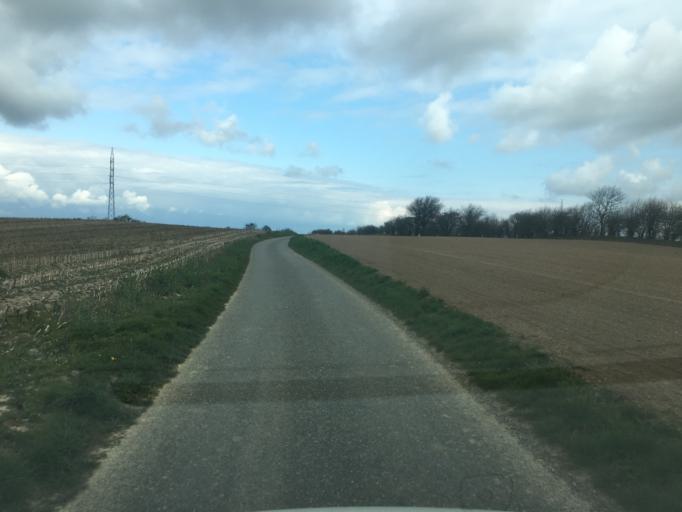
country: DK
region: South Denmark
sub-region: Sonderborg Kommune
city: Grasten
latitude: 54.9942
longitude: 9.5272
